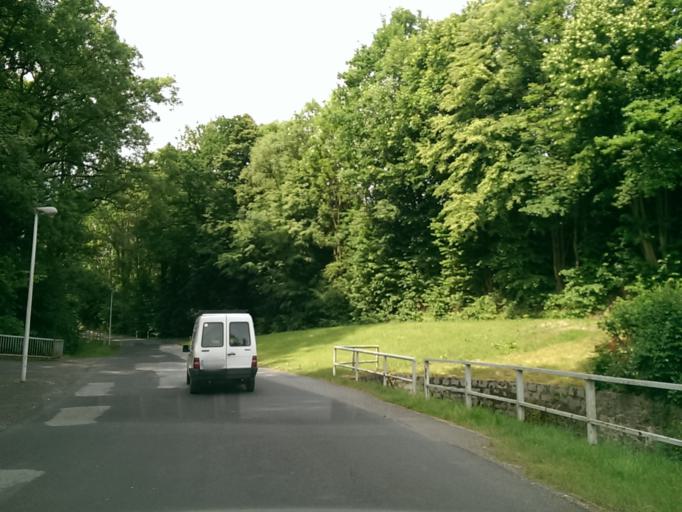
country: DE
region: Saxony
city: Mittelherwigsdorf
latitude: 50.9193
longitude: 14.7657
